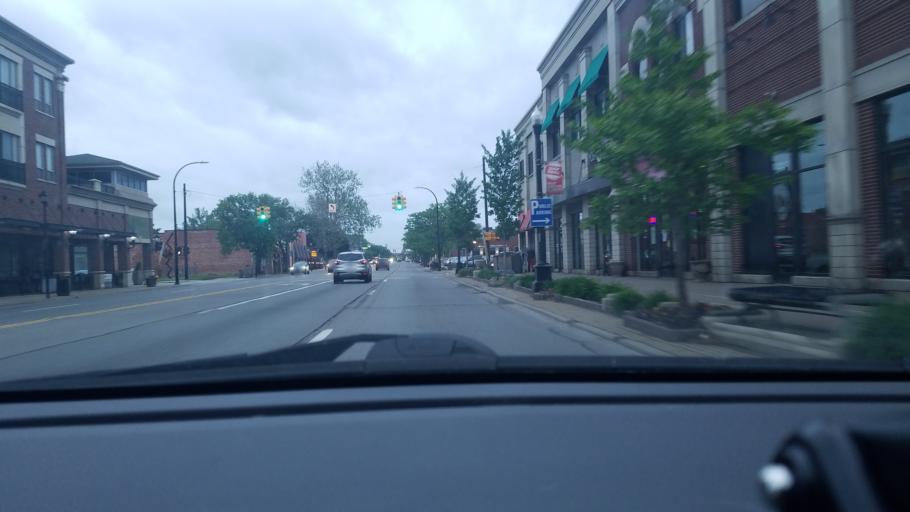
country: US
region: Michigan
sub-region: Wayne County
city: Dearborn Heights
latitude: 42.3055
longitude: -83.2489
